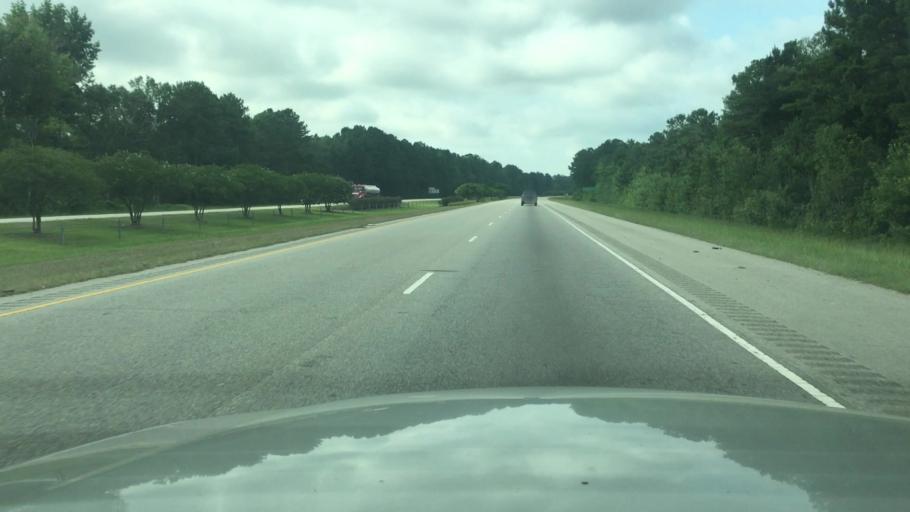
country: US
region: North Carolina
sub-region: Cumberland County
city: Fayetteville
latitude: 35.0001
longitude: -78.8649
